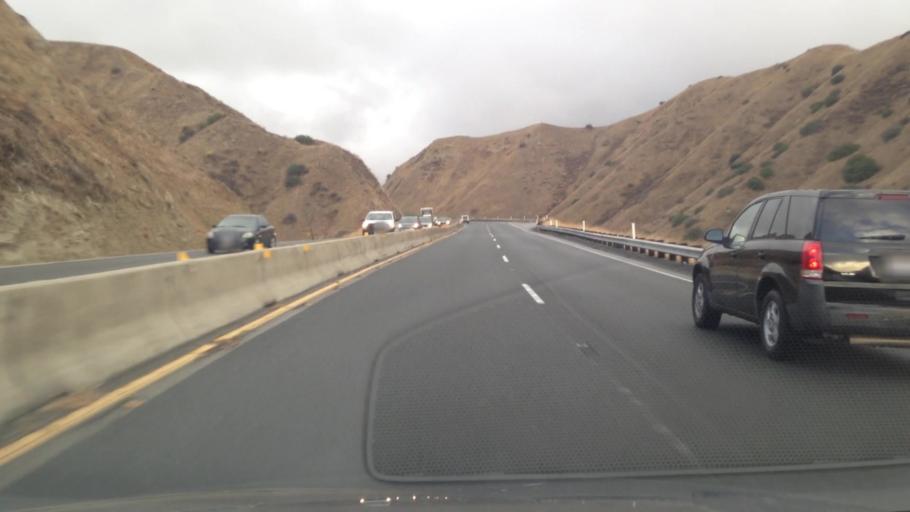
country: US
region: California
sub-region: Riverside County
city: Calimesa
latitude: 33.9395
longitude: -117.0947
